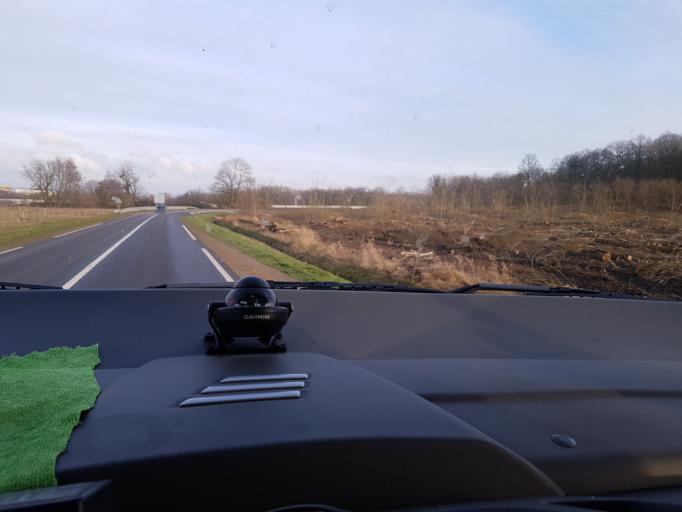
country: FR
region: Champagne-Ardenne
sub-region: Departement des Ardennes
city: Tournes
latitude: 49.7625
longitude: 4.6430
